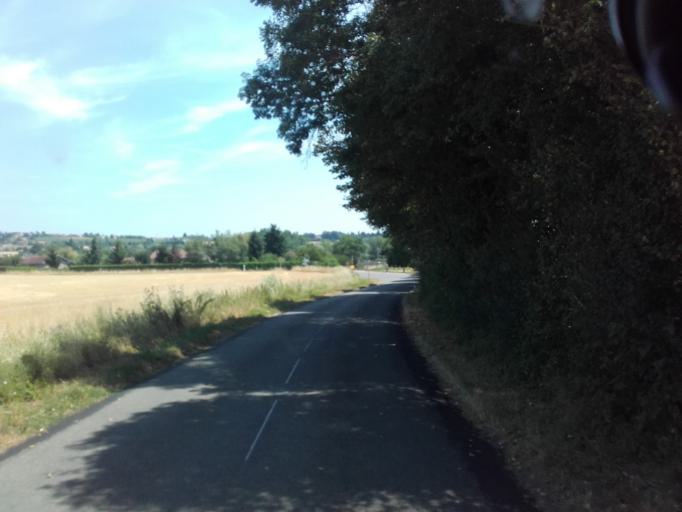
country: FR
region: Bourgogne
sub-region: Departement de Saone-et-Loire
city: Charnay-les-Macon
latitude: 46.2970
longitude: 4.7632
